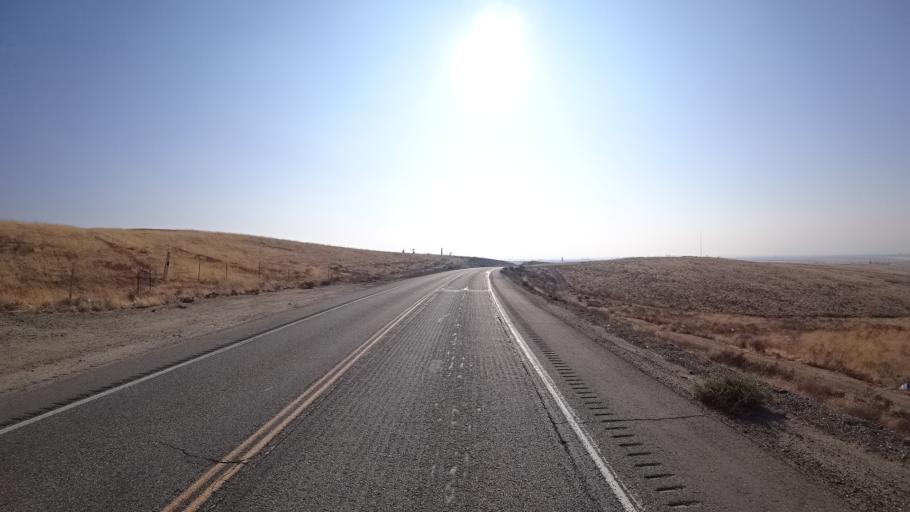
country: US
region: California
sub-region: Kern County
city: Lamont
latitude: 35.3865
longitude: -118.8516
